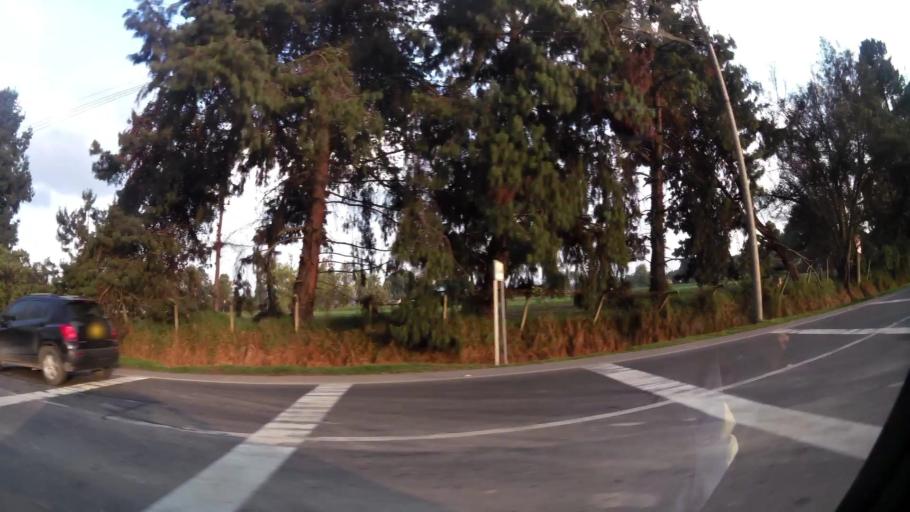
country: CO
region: Cundinamarca
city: Cota
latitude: 4.7989
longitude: -74.1111
